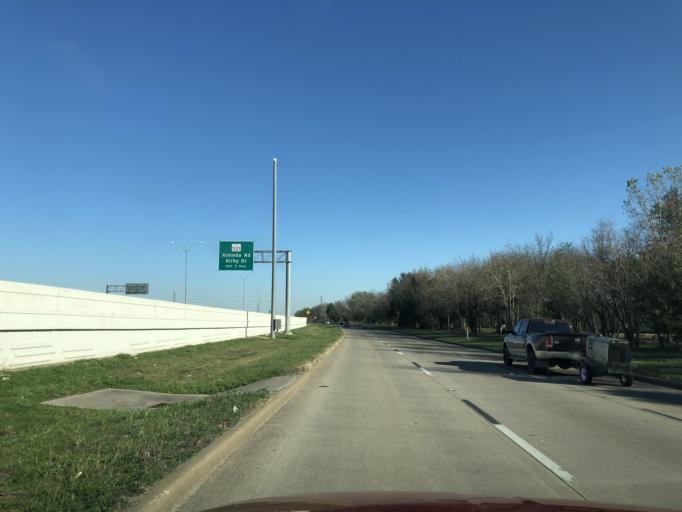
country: US
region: Texas
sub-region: Fort Bend County
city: Fresno
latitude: 29.5965
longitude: -95.4560
